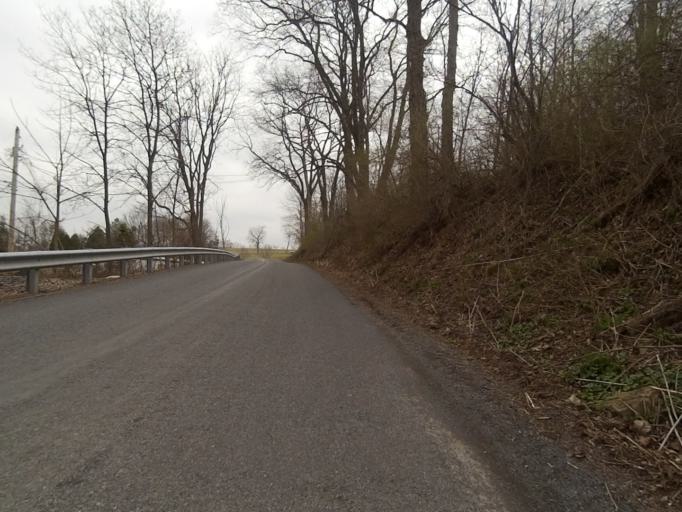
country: US
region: Pennsylvania
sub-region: Centre County
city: Boalsburg
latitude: 40.7925
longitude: -77.7879
